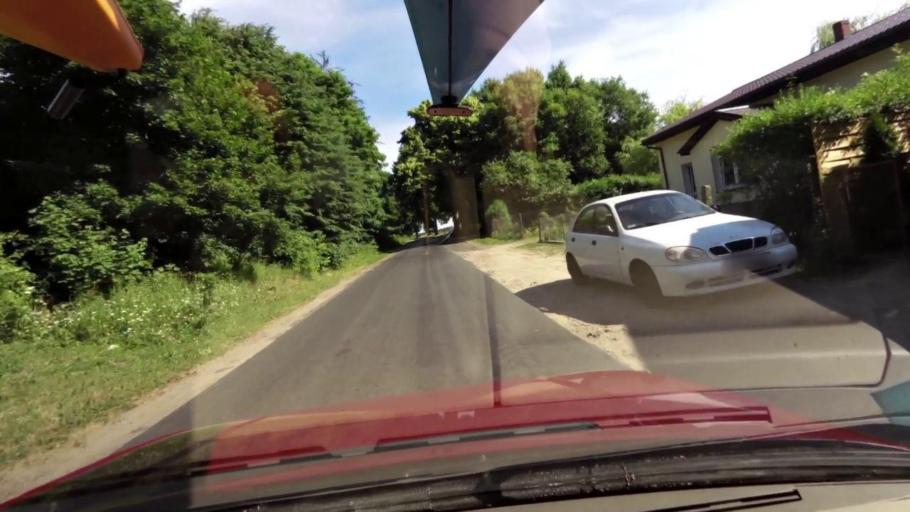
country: PL
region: Pomeranian Voivodeship
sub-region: Powiat bytowski
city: Miastko
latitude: 54.1188
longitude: 16.9477
